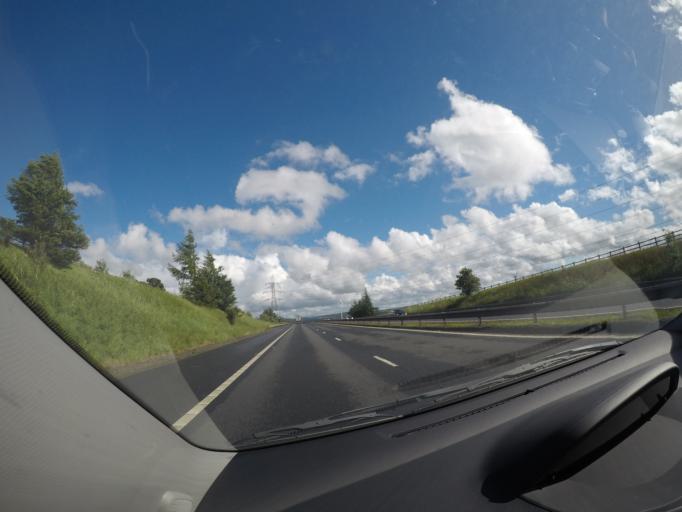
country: GB
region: Scotland
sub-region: South Lanarkshire
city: Lesmahagow
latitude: 55.6119
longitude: -3.8463
